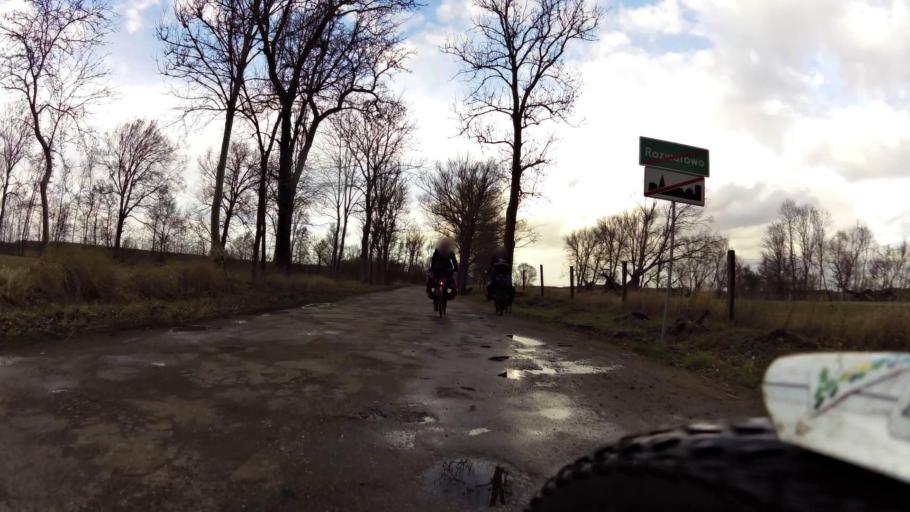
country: PL
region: West Pomeranian Voivodeship
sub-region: Powiat kamienski
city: Kamien Pomorski
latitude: 53.8973
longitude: 14.7307
